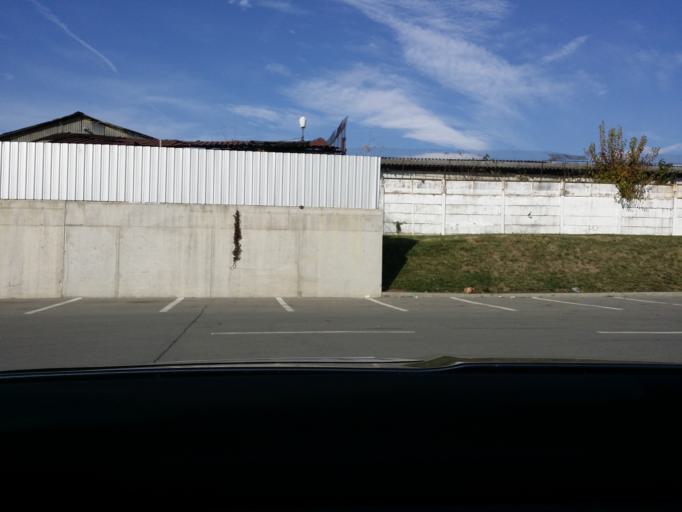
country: RO
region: Prahova
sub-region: Municipiul Campina
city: Campina
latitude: 45.1170
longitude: 25.7457
